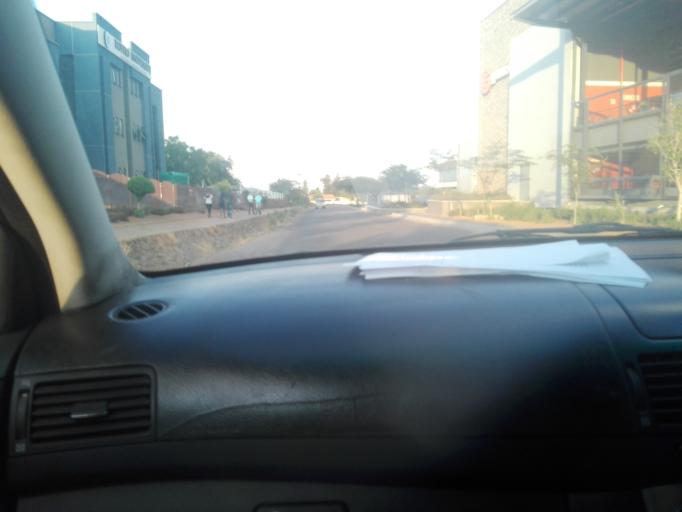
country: BW
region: South East
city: Gaborone
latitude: -24.6853
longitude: 25.8784
